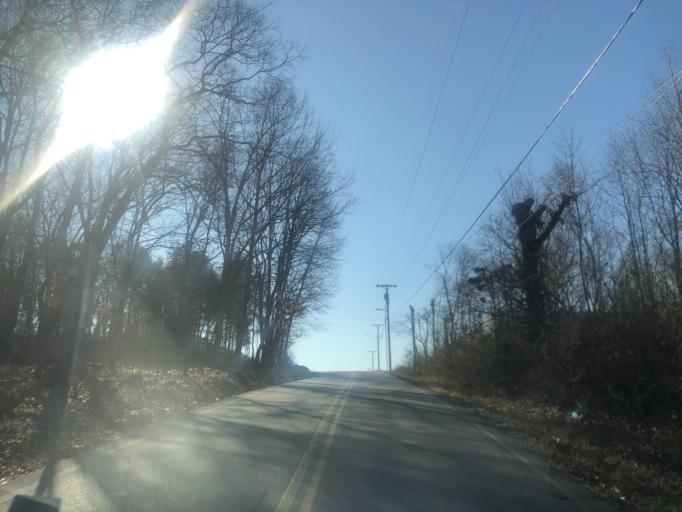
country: US
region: Tennessee
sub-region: Rutherford County
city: La Vergne
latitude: 36.0077
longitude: -86.5832
